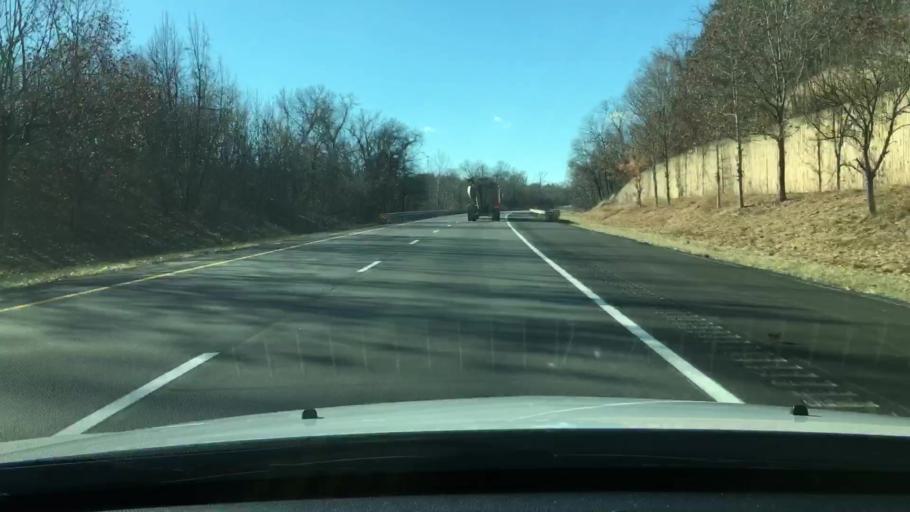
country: US
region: Illinois
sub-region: Pike County
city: Griggsville
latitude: 39.6829
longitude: -90.6556
